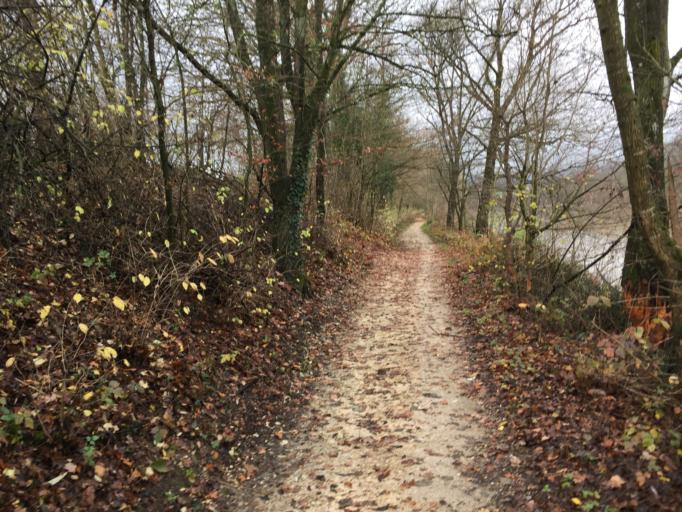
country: CH
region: Solothurn
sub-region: Bezirk Wasseramt
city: Deitingen
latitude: 47.2291
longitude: 7.6184
